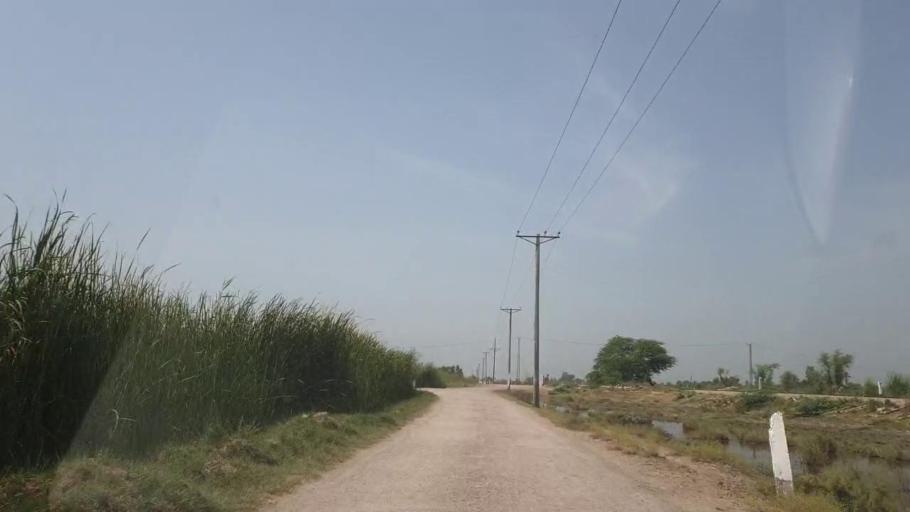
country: PK
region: Sindh
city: Gambat
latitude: 27.3257
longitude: 68.5389
